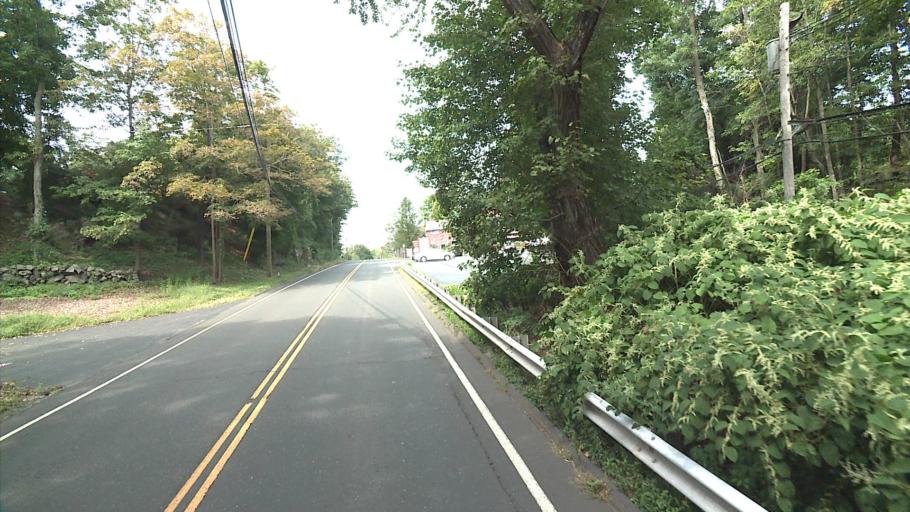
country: US
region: Connecticut
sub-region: Fairfield County
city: North Stamford
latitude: 41.1511
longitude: -73.5921
